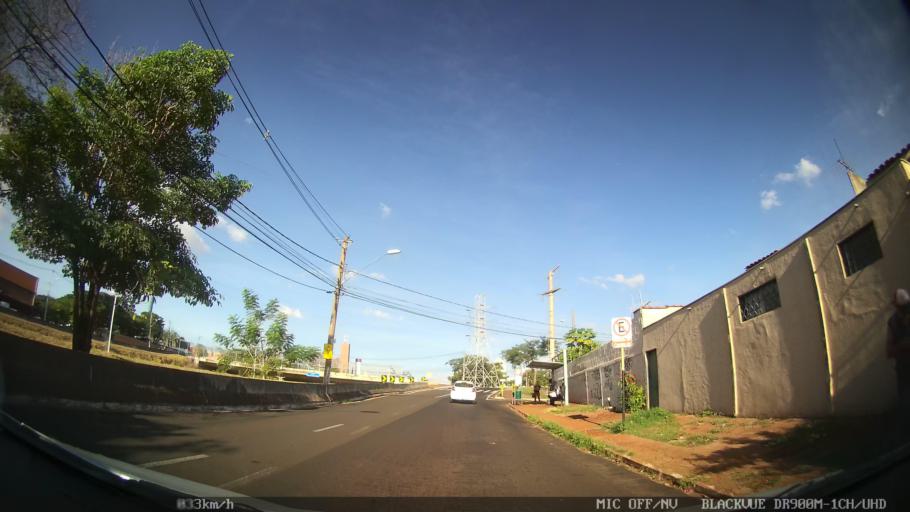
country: BR
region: Sao Paulo
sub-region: Ribeirao Preto
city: Ribeirao Preto
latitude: -21.1929
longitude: -47.7775
